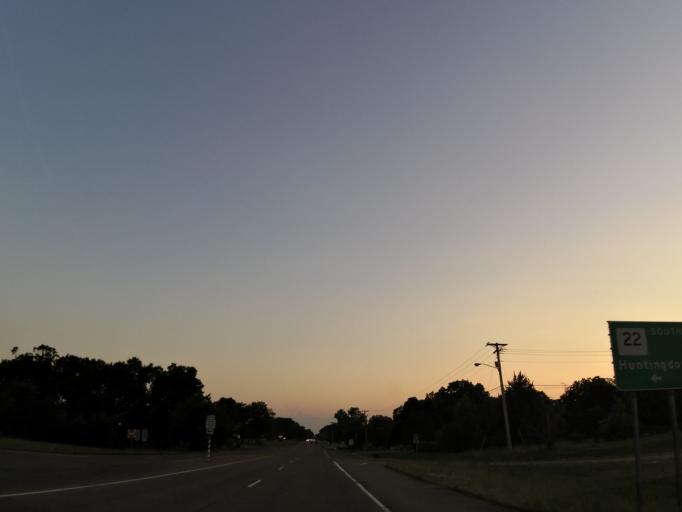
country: US
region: Tennessee
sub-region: Carroll County
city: McKenzie
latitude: 36.1405
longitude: -88.4899
